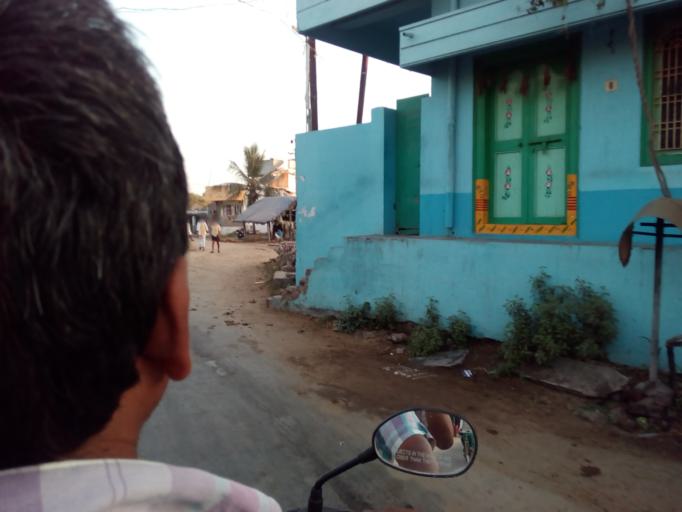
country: IN
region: Andhra Pradesh
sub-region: Prakasam
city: Vetapalem
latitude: 15.7267
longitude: 80.2541
